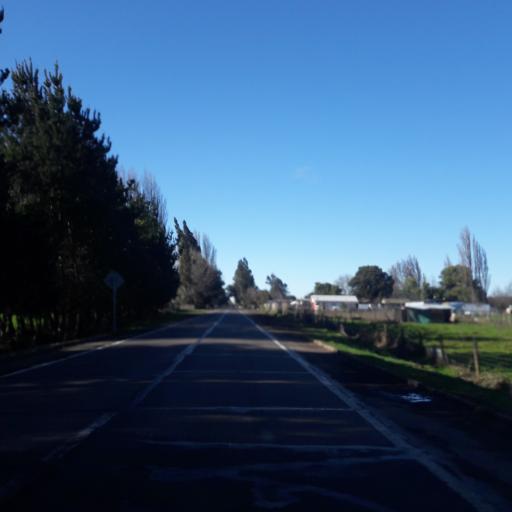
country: CL
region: Araucania
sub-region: Provincia de Malleco
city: Angol
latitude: -37.7595
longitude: -72.5722
